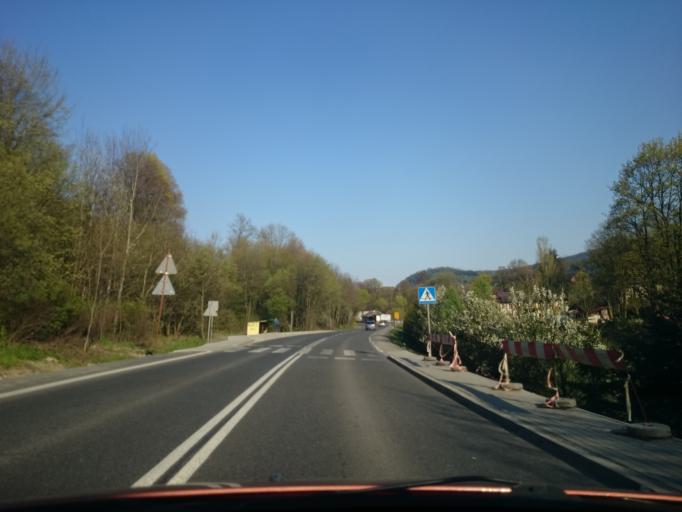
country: PL
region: Lower Silesian Voivodeship
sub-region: Powiat klodzki
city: Szczytna
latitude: 50.4086
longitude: 16.4259
